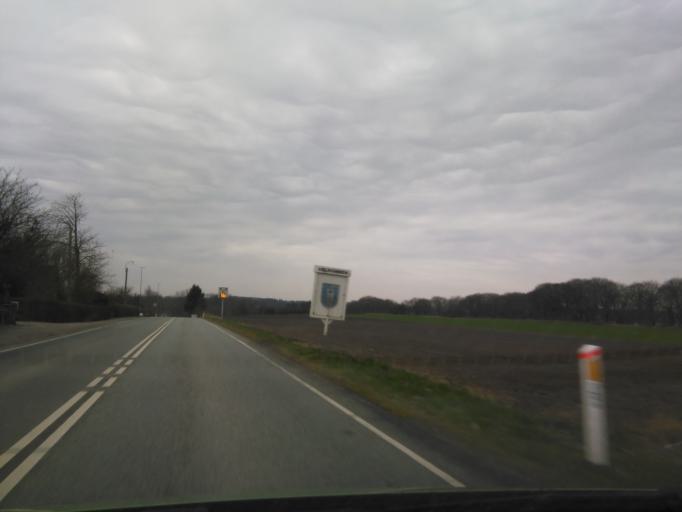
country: DK
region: North Denmark
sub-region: Mariagerfjord Kommune
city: Mariager
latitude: 56.6613
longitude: 9.9947
